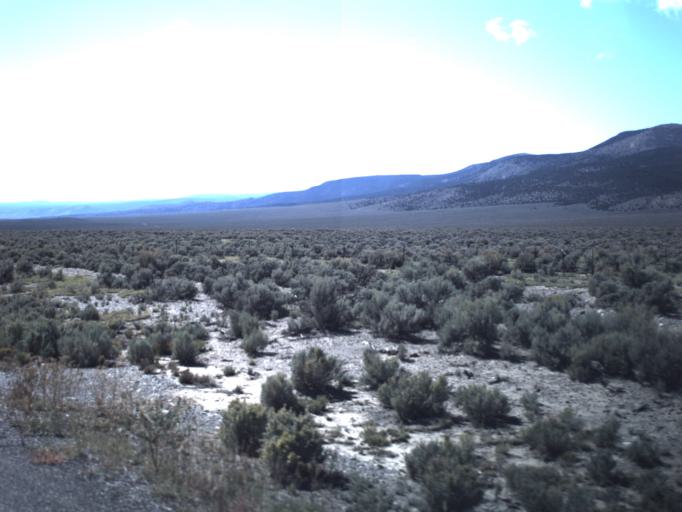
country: US
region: Utah
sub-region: Piute County
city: Junction
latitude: 38.2663
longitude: -111.9865
